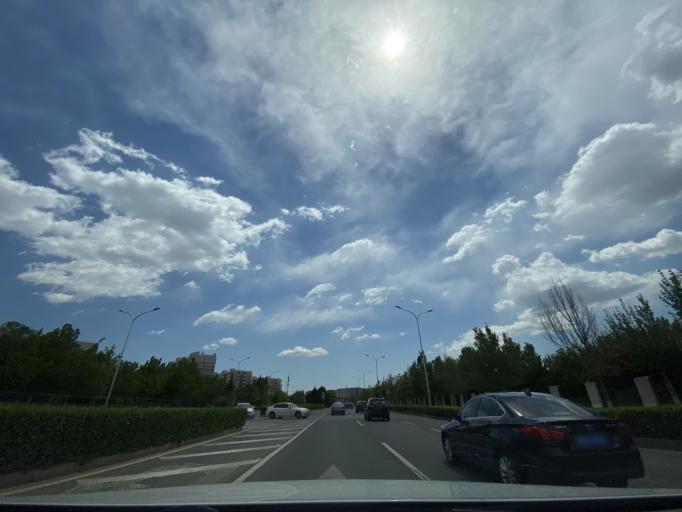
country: CN
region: Beijing
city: Sijiqing
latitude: 39.9372
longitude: 116.2413
